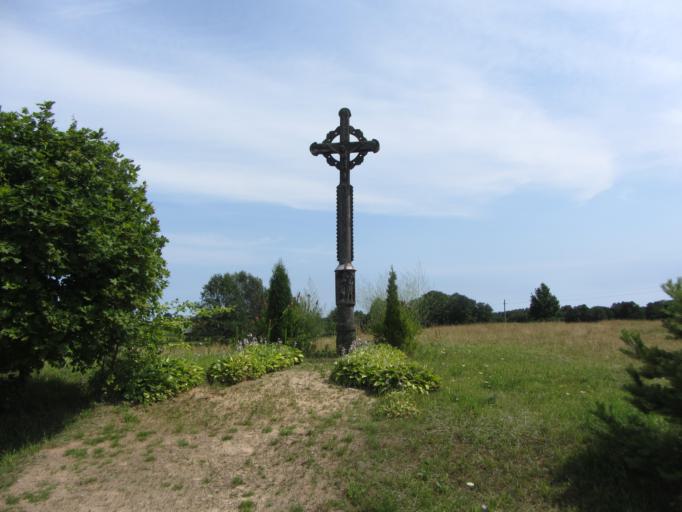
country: LT
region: Alytaus apskritis
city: Druskininkai
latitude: 54.0781
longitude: 23.9784
